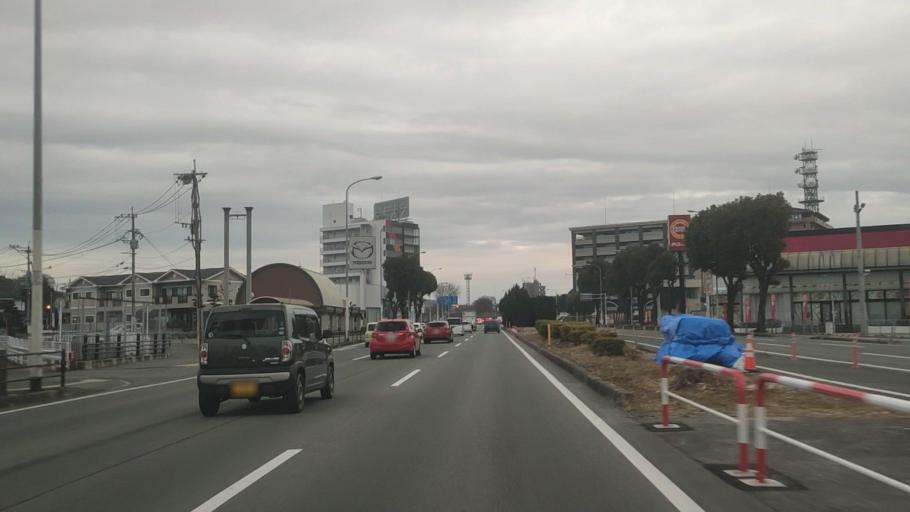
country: JP
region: Kumamoto
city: Kumamoto
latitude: 32.8136
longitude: 130.7500
